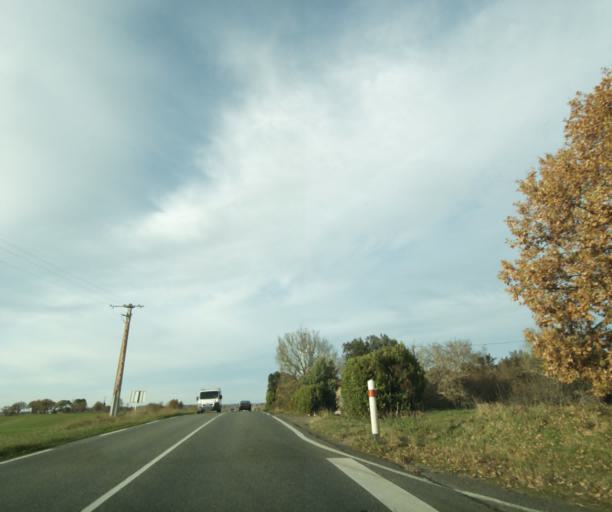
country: FR
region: Midi-Pyrenees
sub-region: Departement du Gers
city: Eauze
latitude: 43.7769
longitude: 0.1227
